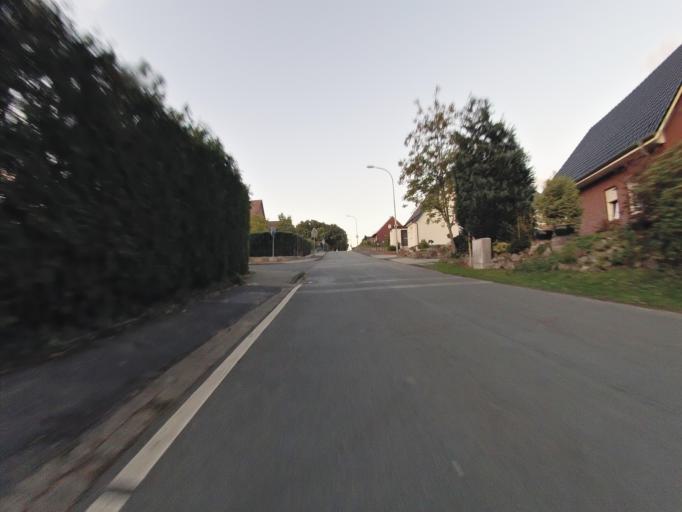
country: DE
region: North Rhine-Westphalia
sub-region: Regierungsbezirk Munster
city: Tecklenburg
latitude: 52.2552
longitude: 7.7865
